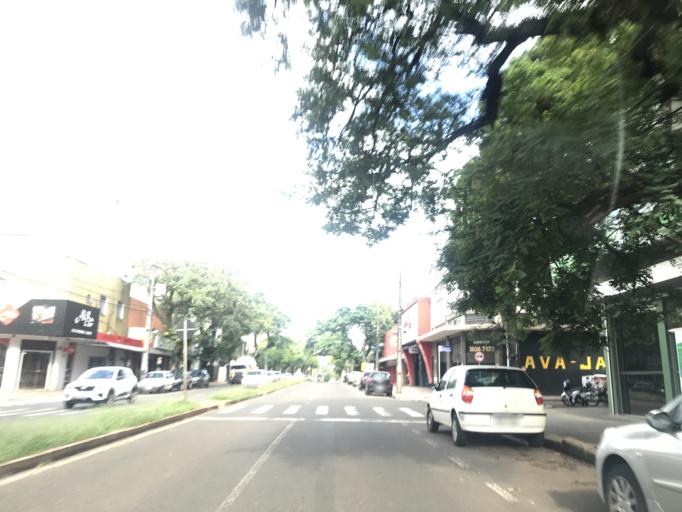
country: BR
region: Parana
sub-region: Maringa
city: Maringa
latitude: -23.4235
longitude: -51.9565
